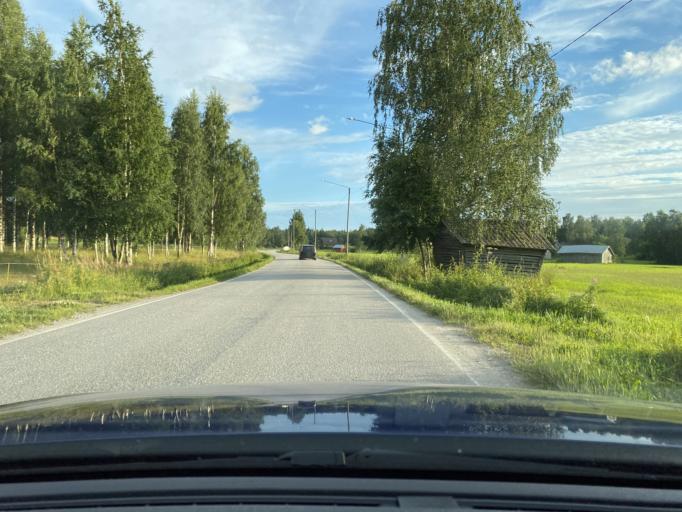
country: FI
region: Ostrobothnia
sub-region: Vaasa
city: Korsnaes
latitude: 62.9646
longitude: 21.1906
